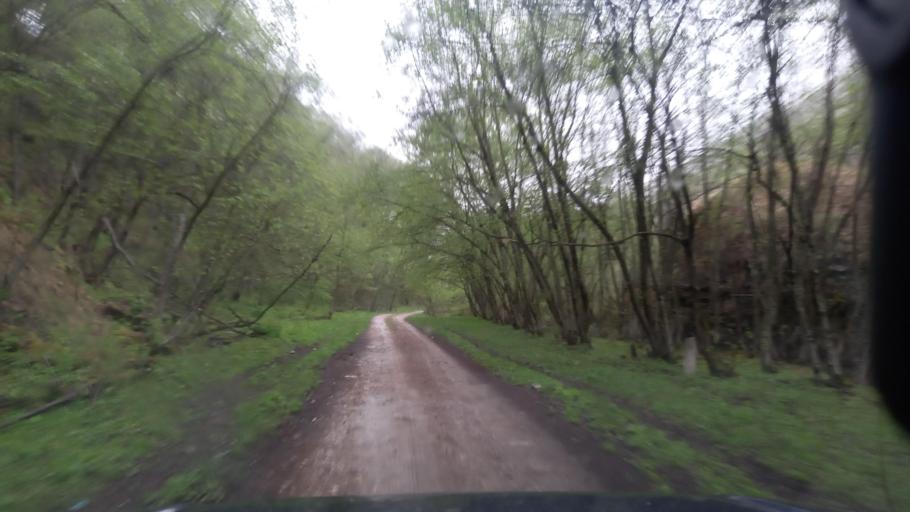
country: RU
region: Kabardino-Balkariya
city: Bylym
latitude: 43.5997
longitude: 42.9274
